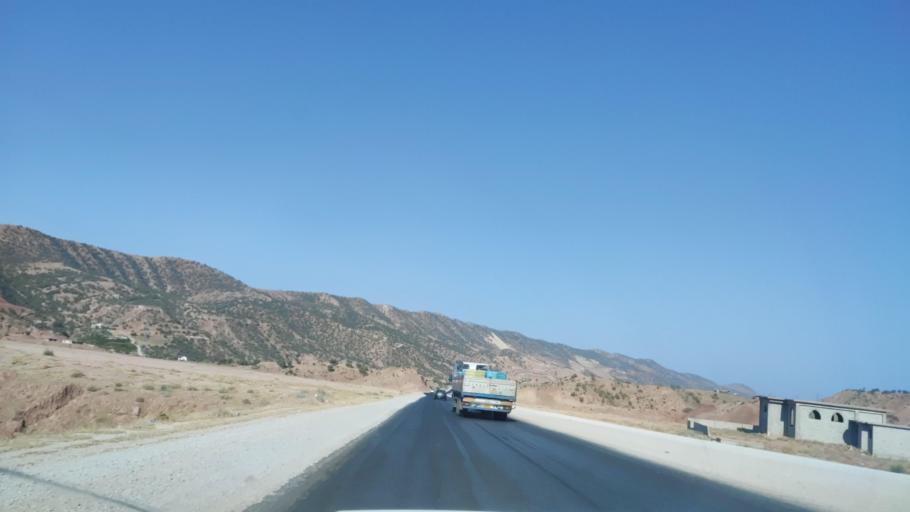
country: IQ
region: Arbil
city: Shaqlawah
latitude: 36.4298
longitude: 44.3383
